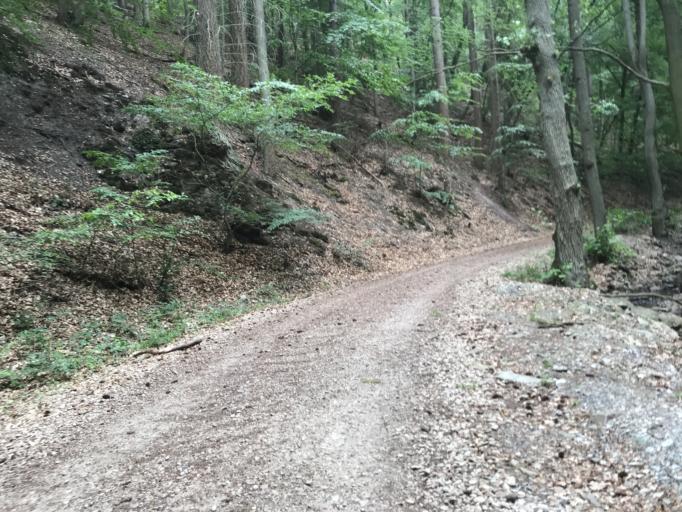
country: DE
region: Rheinland-Pfalz
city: Trechtingshausen
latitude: 49.9894
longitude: 7.8462
